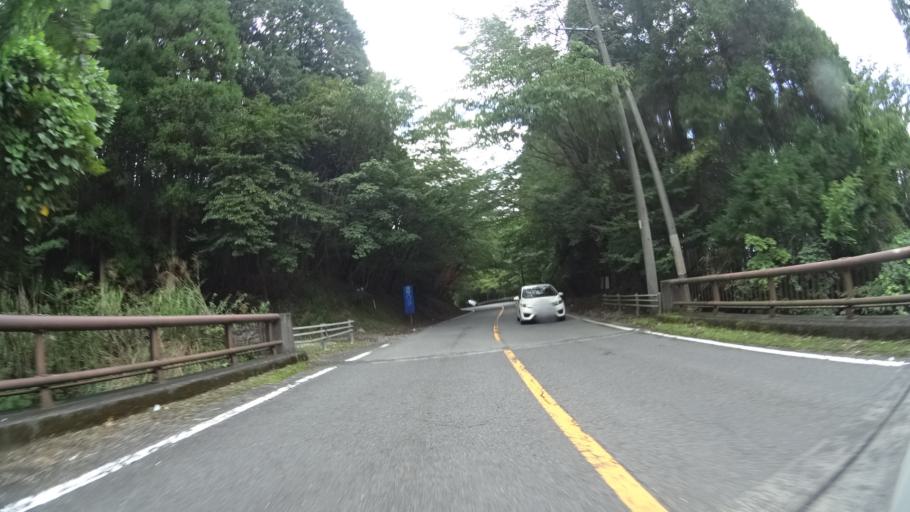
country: JP
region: Oita
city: Beppu
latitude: 33.2800
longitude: 131.3704
